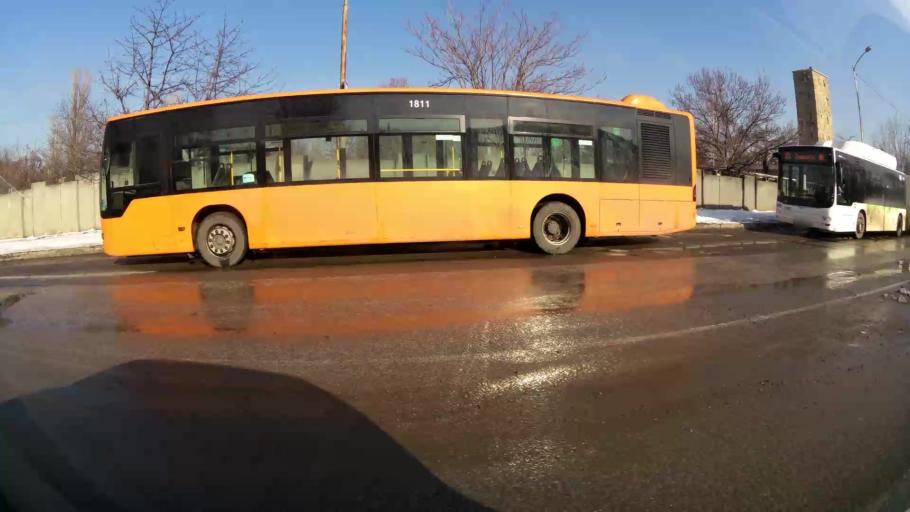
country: BG
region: Sofia-Capital
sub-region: Stolichna Obshtina
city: Sofia
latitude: 42.6588
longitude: 23.3280
